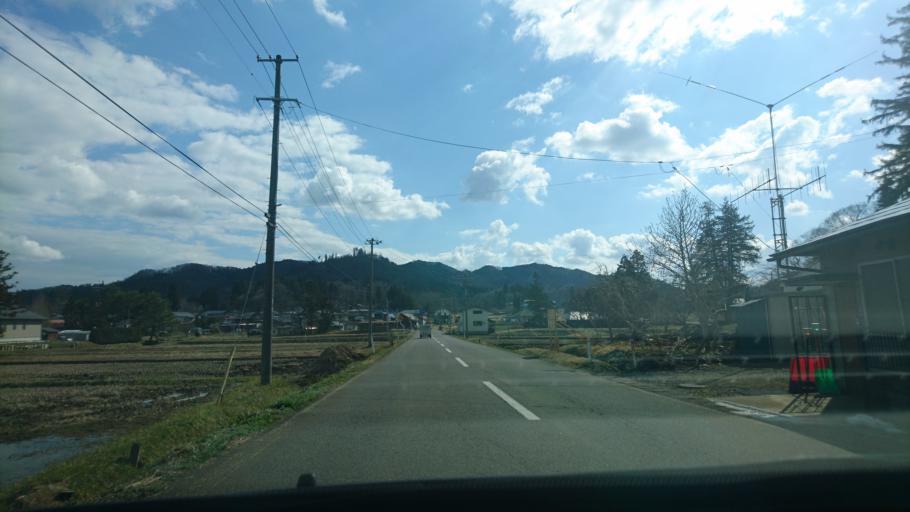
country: JP
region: Iwate
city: Kitakami
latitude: 39.2993
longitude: 141.2027
